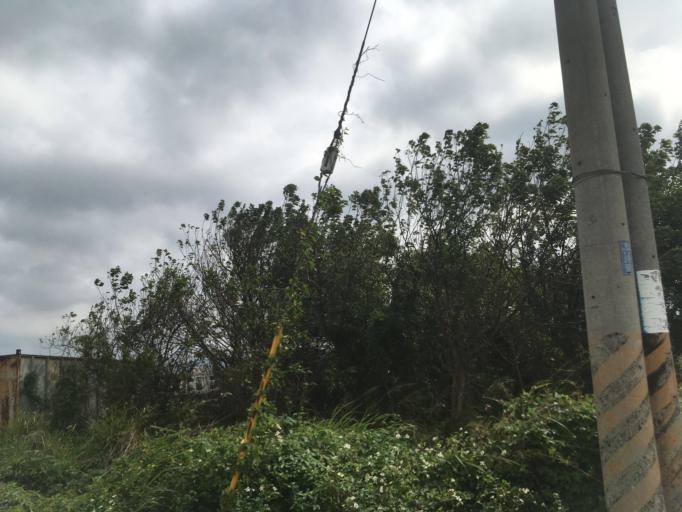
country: TW
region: Taiwan
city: Fengyuan
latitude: 24.4058
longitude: 120.6734
